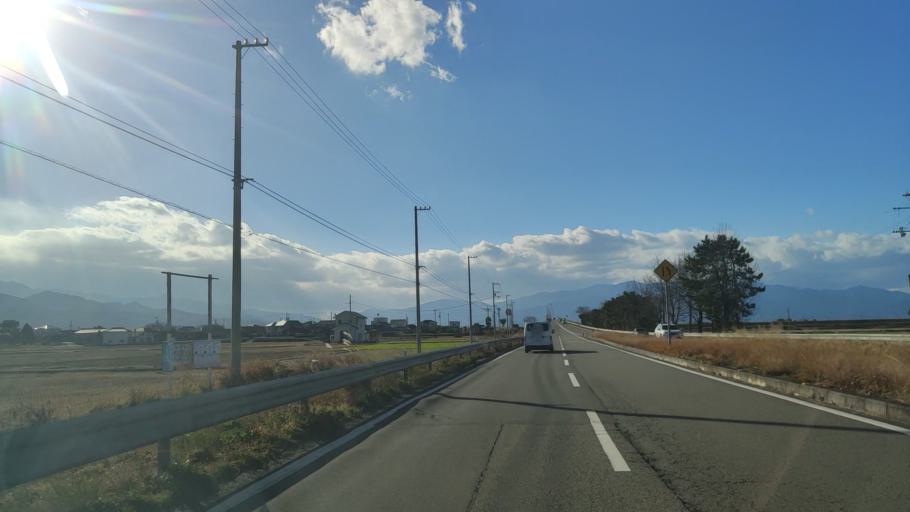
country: JP
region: Ehime
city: Saijo
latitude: 33.9191
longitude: 133.1605
